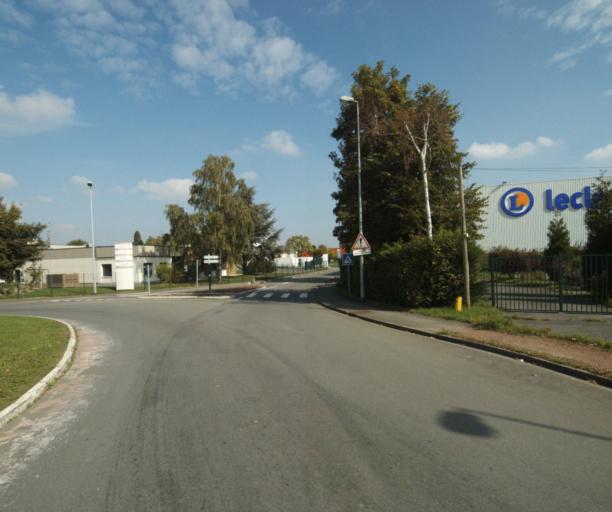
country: FR
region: Nord-Pas-de-Calais
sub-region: Departement du Nord
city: Seclin
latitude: 50.5608
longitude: 3.0291
